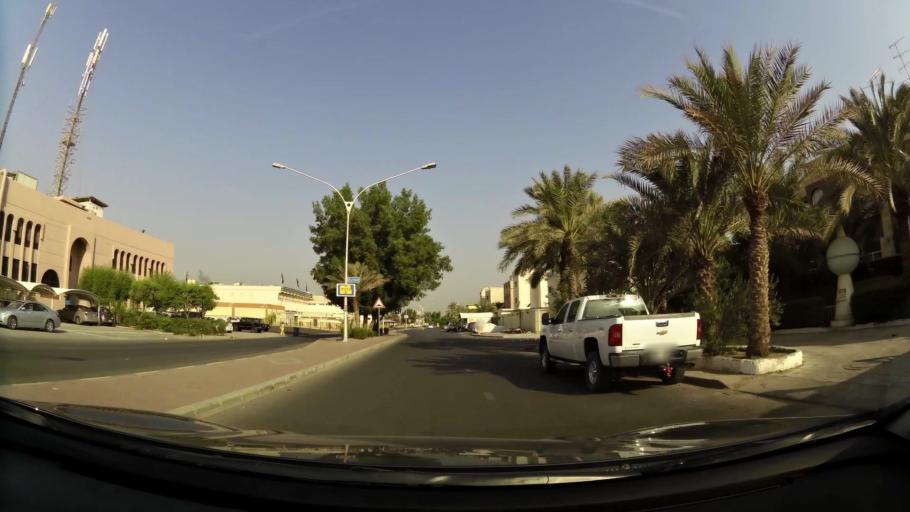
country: KW
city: Bayan
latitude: 29.3165
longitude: 48.0445
